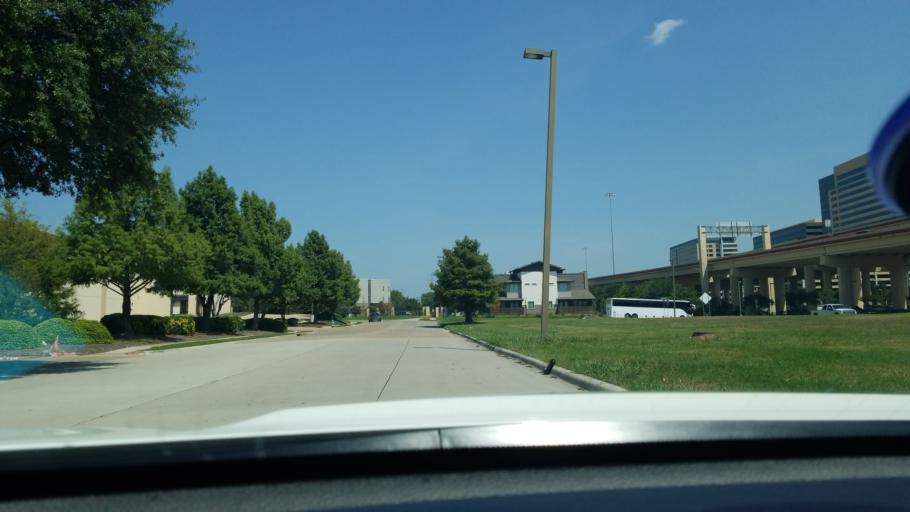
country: US
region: Texas
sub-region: Collin County
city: Plano
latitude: 33.0052
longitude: -96.7060
